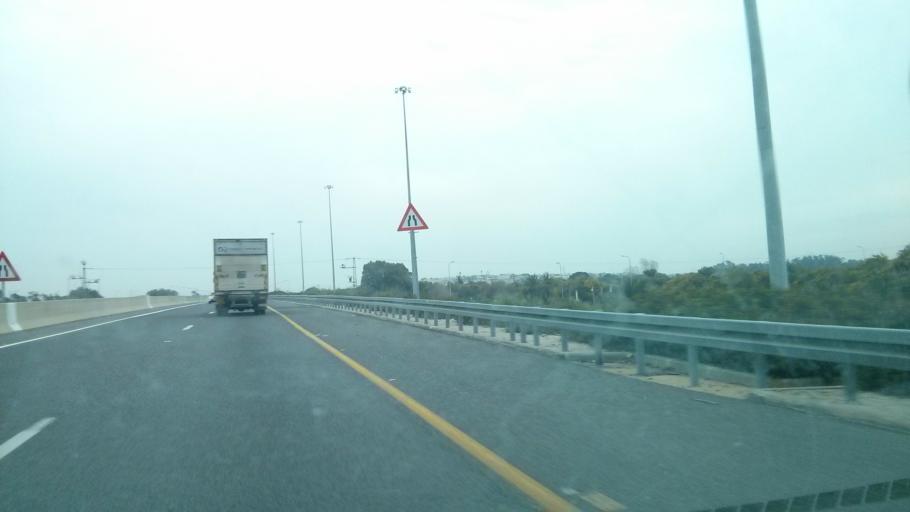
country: IL
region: Haifa
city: Qesarya
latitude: 32.5067
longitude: 34.9135
